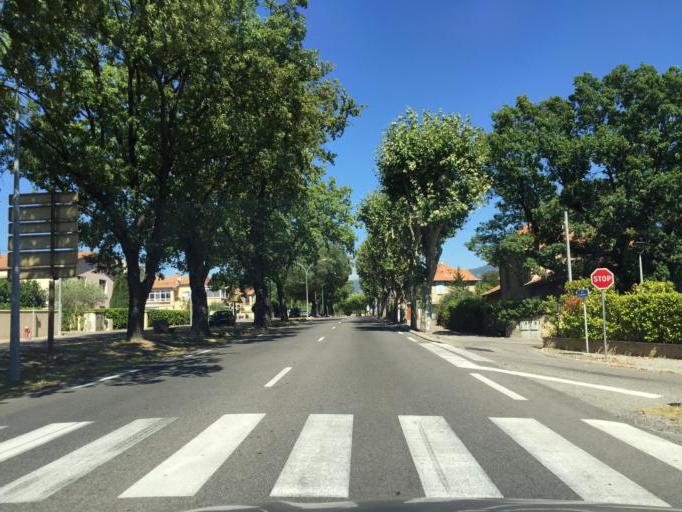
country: FR
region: Provence-Alpes-Cote d'Azur
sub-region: Departement des Alpes-de-Haute-Provence
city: Volonne
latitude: 44.0749
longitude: 5.9928
